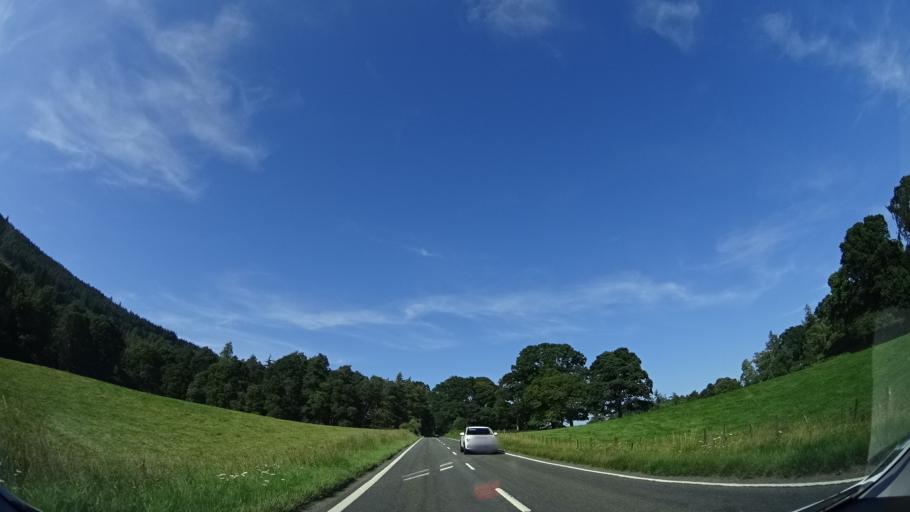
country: GB
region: Scotland
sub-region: Highland
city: Inverness
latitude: 57.4416
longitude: -4.2969
